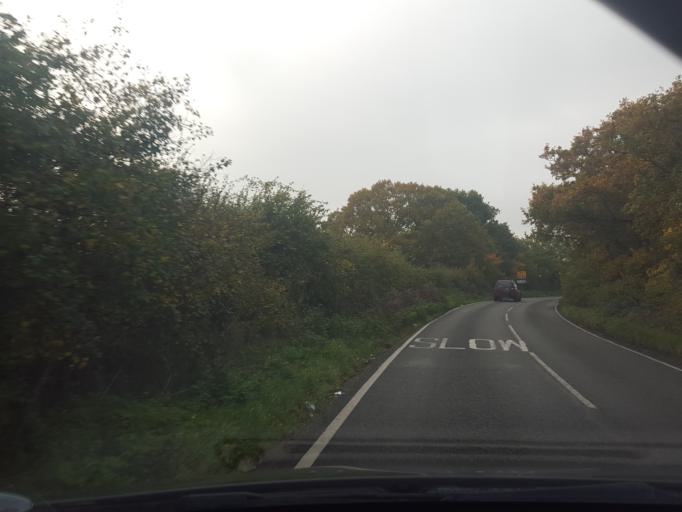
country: GB
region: England
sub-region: Essex
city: Little Clacton
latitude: 51.8146
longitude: 1.1270
